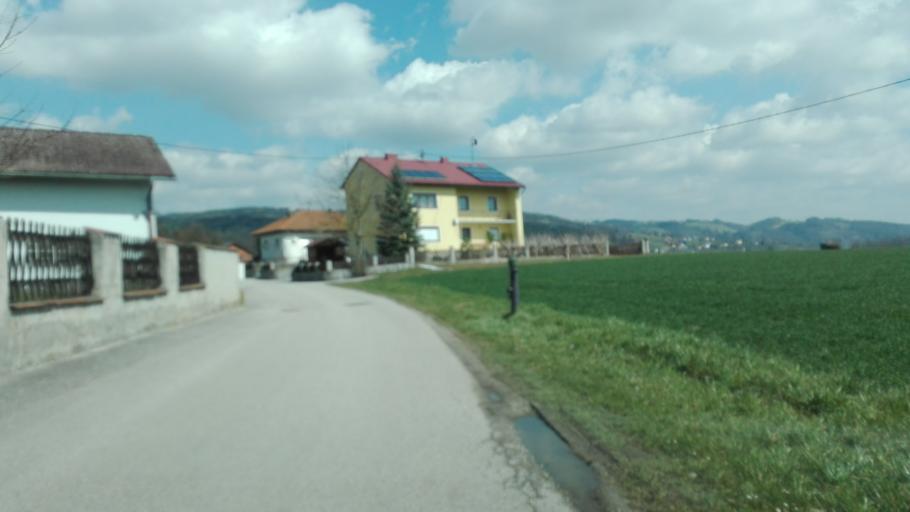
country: AT
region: Upper Austria
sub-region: Politischer Bezirk Urfahr-Umgebung
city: Feldkirchen an der Donau
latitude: 48.3531
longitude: 14.0273
